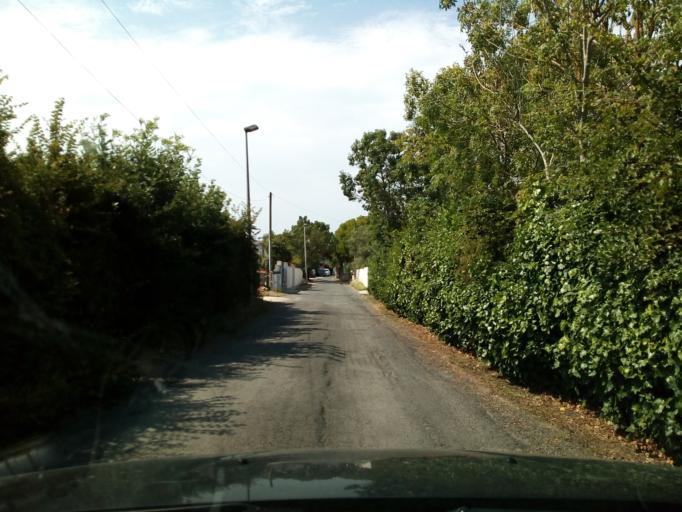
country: FR
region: Poitou-Charentes
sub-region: Departement de la Charente-Maritime
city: Dolus-d'Oleron
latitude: 45.9453
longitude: -1.3025
